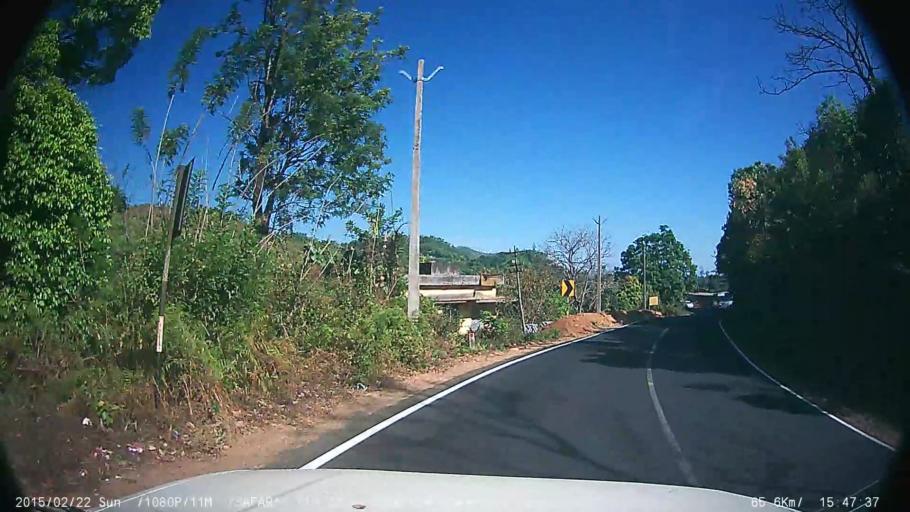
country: IN
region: Kerala
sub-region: Kottayam
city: Erattupetta
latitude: 9.5767
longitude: 76.9912
